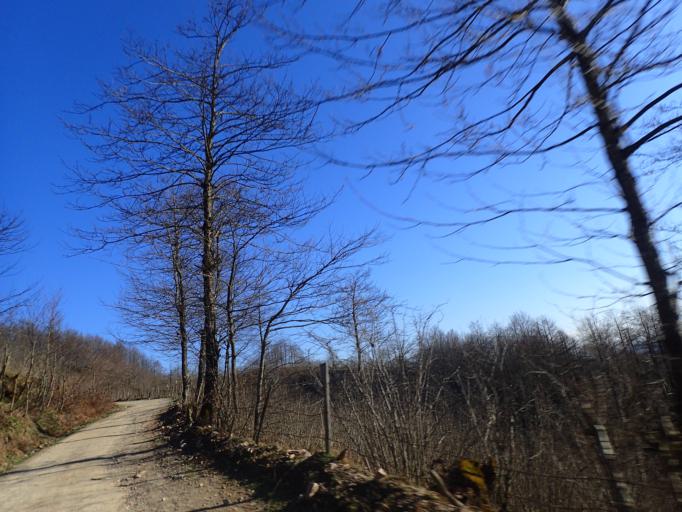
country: TR
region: Ordu
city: Camas
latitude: 40.8539
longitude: 37.5048
